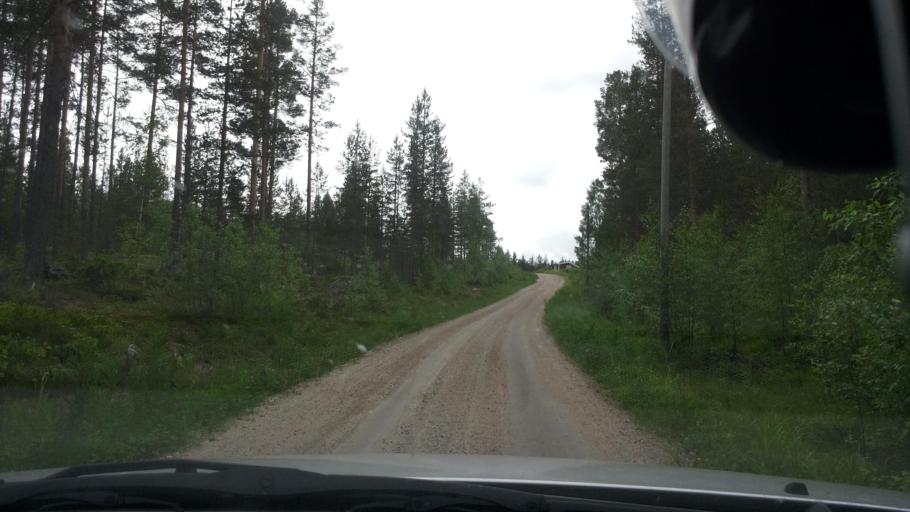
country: SE
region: Gaevleborg
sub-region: Ovanakers Kommun
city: Edsbyn
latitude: 61.5013
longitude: 15.3379
